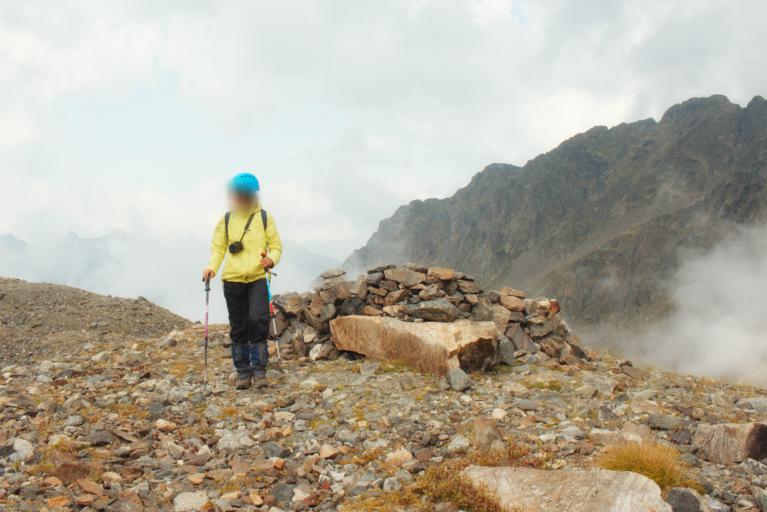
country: RU
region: Karachayevo-Cherkesiya
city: Nizhniy Arkhyz
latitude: 43.4292
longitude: 41.2540
